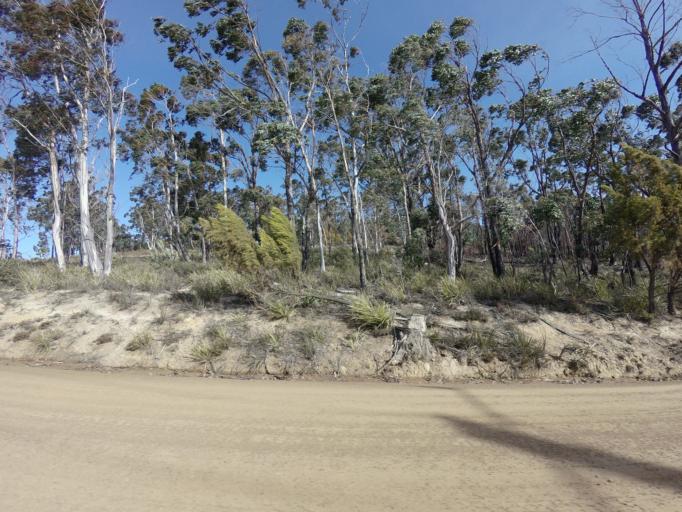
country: AU
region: Tasmania
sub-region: Kingborough
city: Kettering
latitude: -43.0822
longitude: 147.2645
